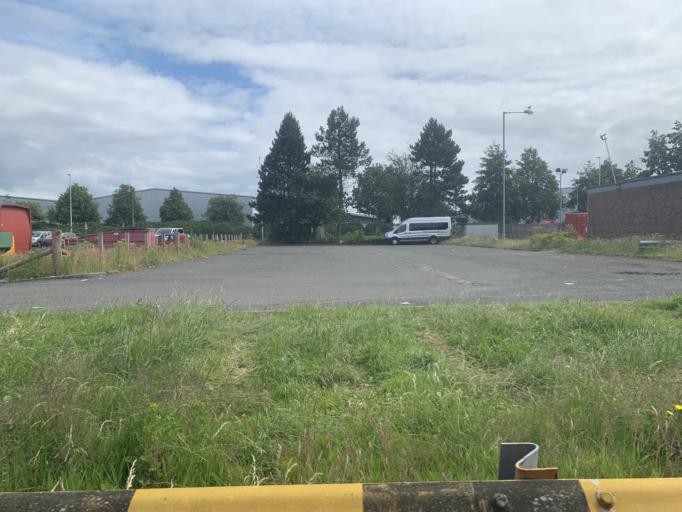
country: GB
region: Scotland
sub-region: Renfrewshire
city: Inchinnan
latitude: 55.8659
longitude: -4.4260
